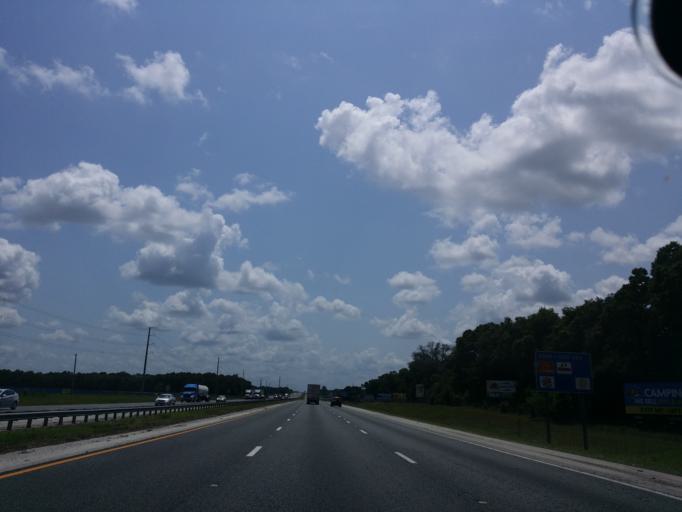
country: US
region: Florida
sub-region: Marion County
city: Ocala
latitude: 29.2179
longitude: -82.1846
